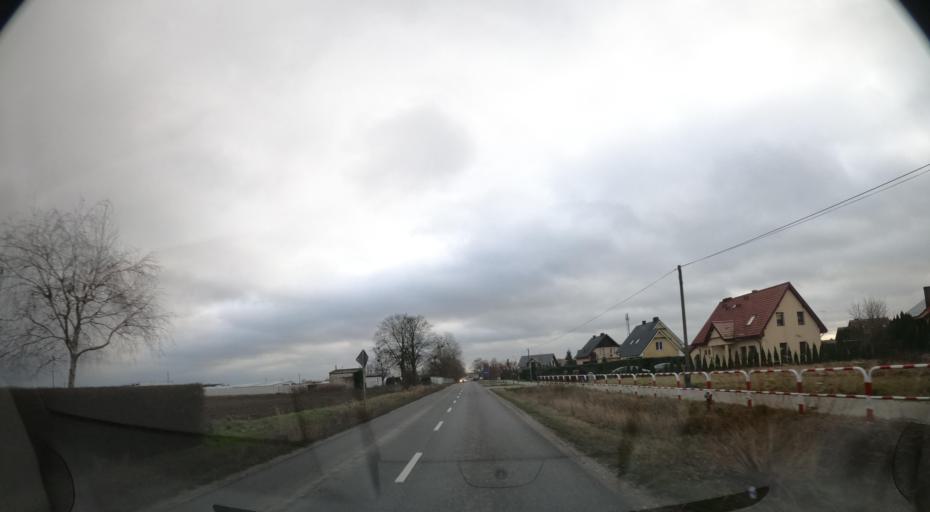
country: PL
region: Kujawsko-Pomorskie
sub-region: Powiat nakielski
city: Sadki
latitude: 53.1642
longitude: 17.4429
